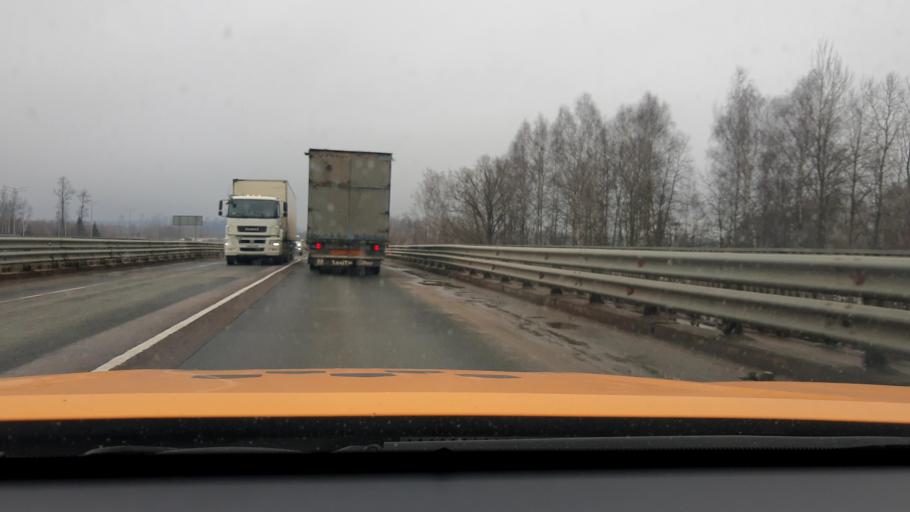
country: RU
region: Moskovskaya
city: Krasnoarmeysk
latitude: 56.0473
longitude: 38.1535
